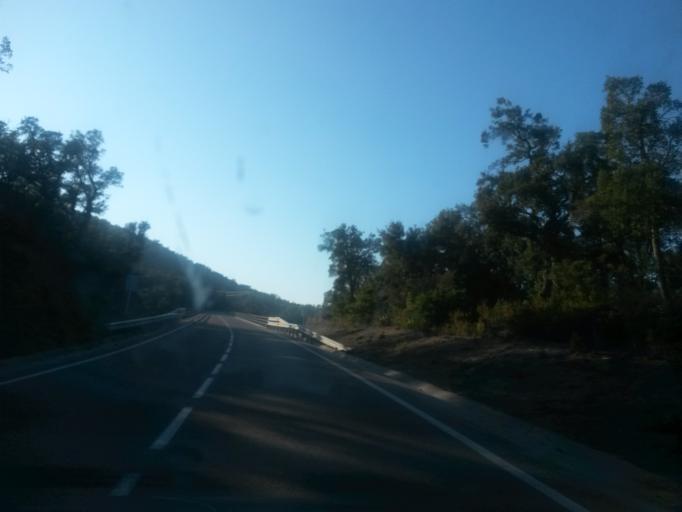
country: ES
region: Catalonia
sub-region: Provincia de Girona
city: Darnius
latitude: 42.3710
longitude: 2.8148
